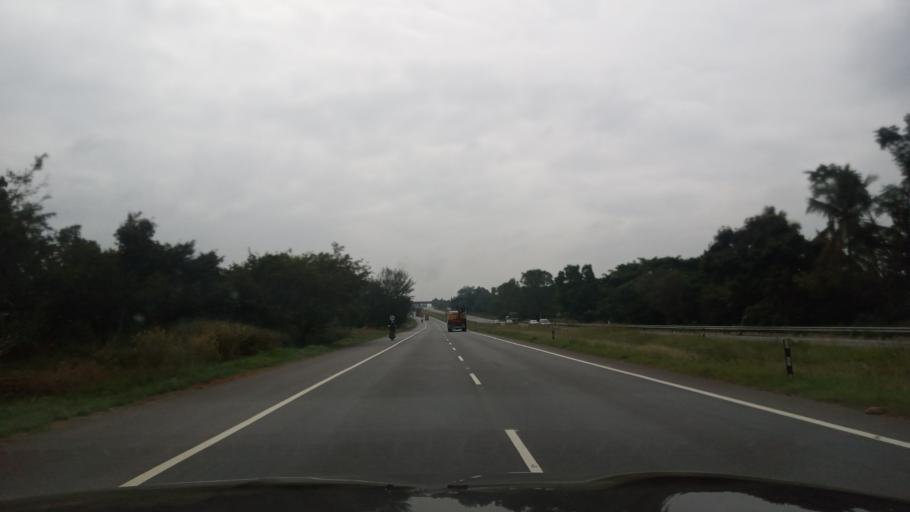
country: IN
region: Karnataka
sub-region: Bangalore Urban
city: Bangalore
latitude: 12.9330
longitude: 77.4695
